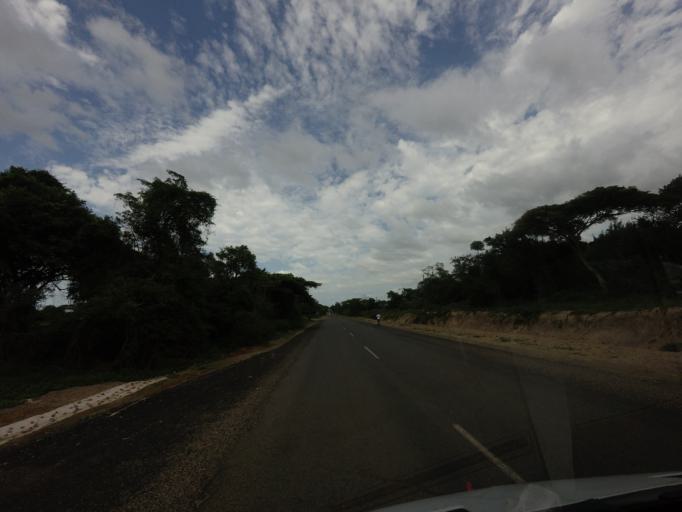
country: ZA
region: KwaZulu-Natal
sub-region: uMkhanyakude District Municipality
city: Mtubatuba
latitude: -28.3797
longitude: 32.3647
